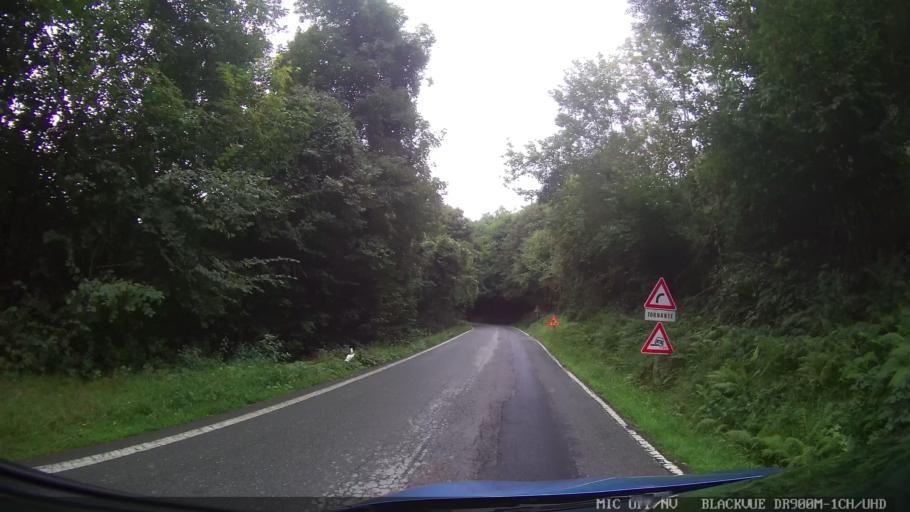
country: IT
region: Piedmont
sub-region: Provincia di Torino
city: Levone
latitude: 45.3298
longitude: 7.6216
